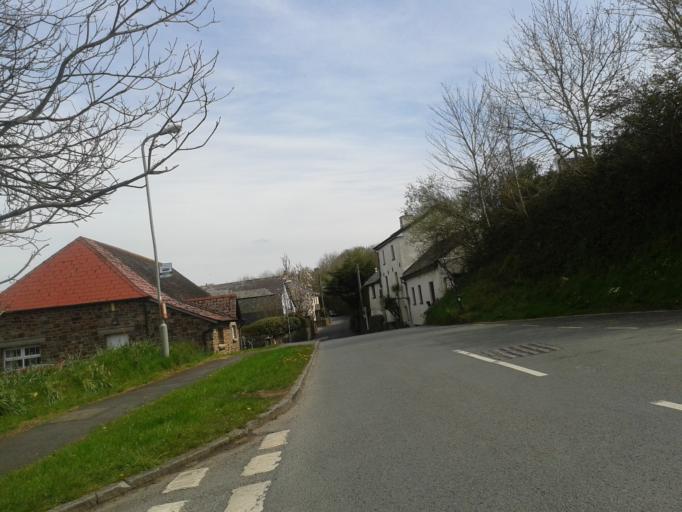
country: GB
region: England
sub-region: Devon
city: Braunton
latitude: 51.1358
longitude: -4.1987
